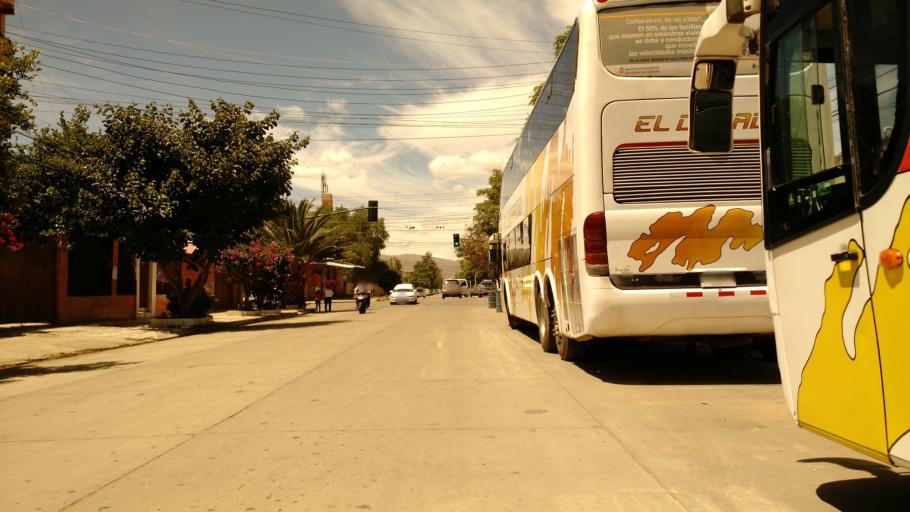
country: BO
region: Cochabamba
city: Cochabamba
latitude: -17.3990
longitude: -66.1665
